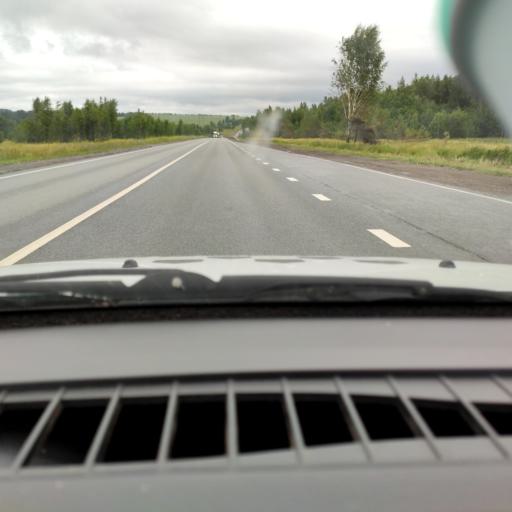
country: RU
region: Tatarstan
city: Yelabuga
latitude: 55.8168
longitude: 52.1594
